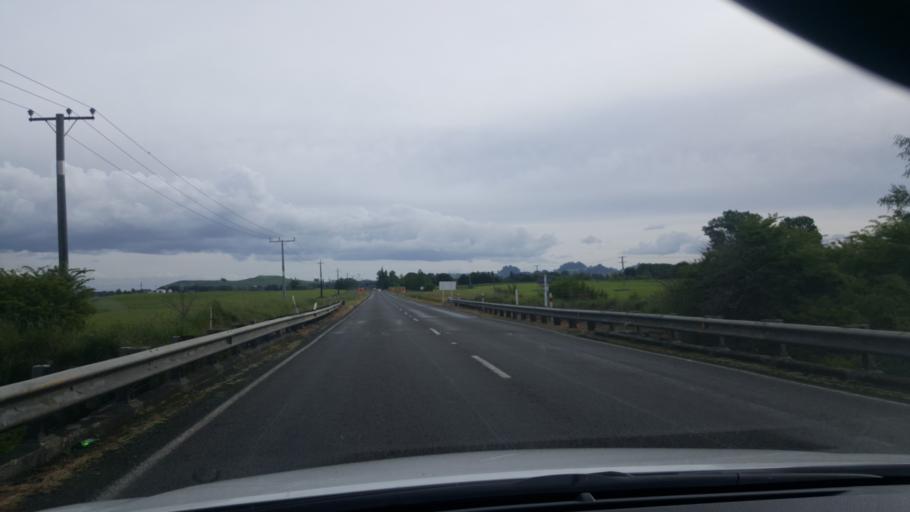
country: NZ
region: Bay of Plenty
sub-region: Rotorua District
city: Rotorua
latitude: -38.4001
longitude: 176.3320
